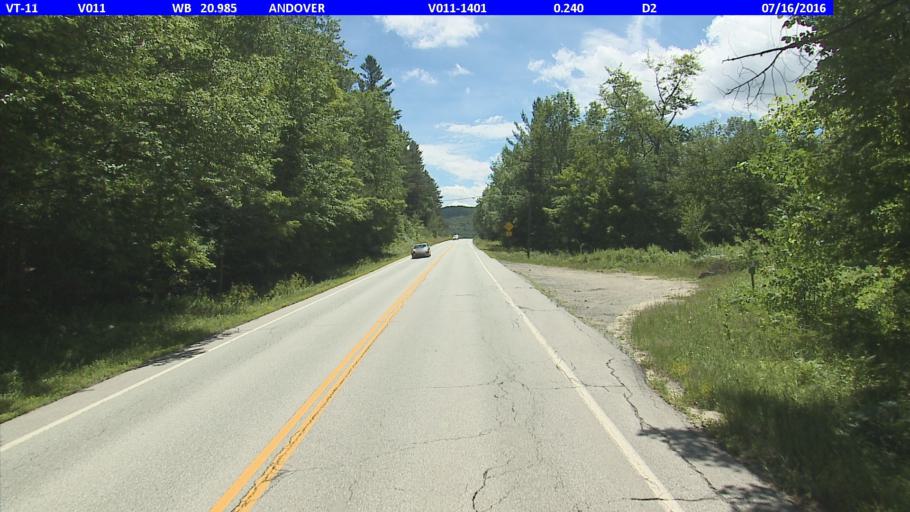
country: US
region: Vermont
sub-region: Windsor County
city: Chester
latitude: 43.2359
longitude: -72.7263
